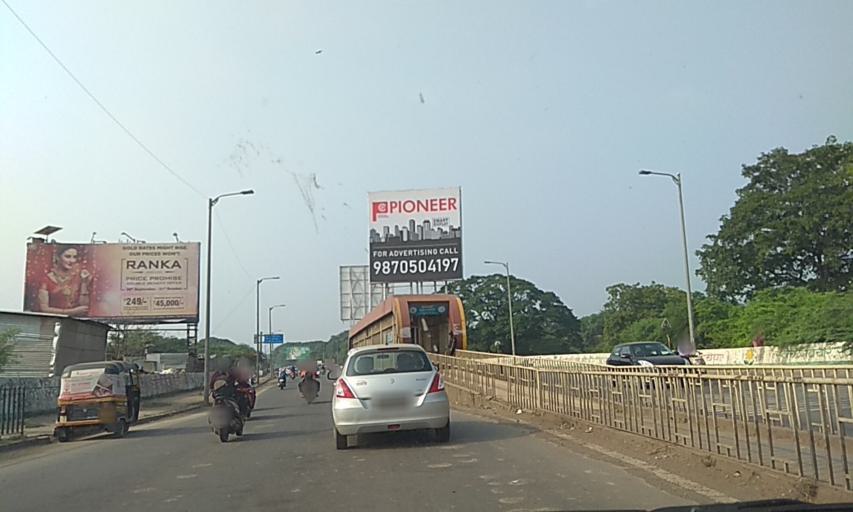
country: IN
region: Maharashtra
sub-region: Pune Division
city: Shivaji Nagar
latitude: 18.5369
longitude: 73.8626
